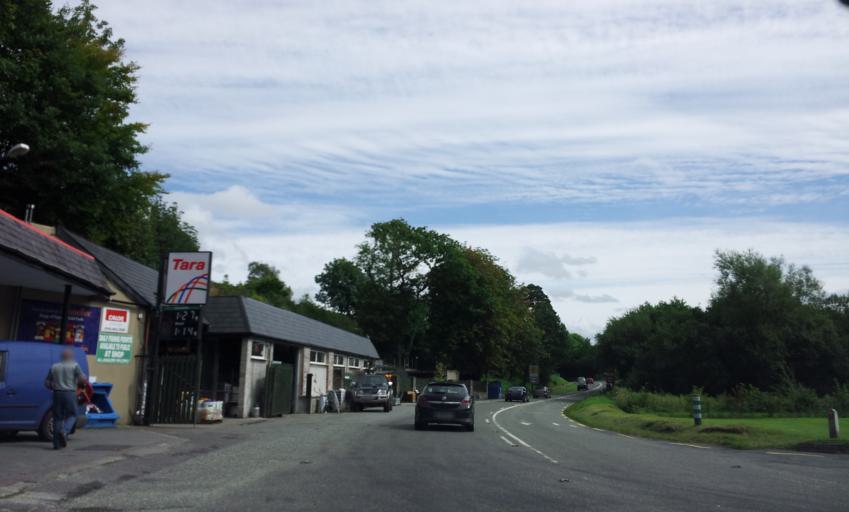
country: IE
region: Munster
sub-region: Ciarrai
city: Cill Airne
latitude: 52.0755
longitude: -9.6325
